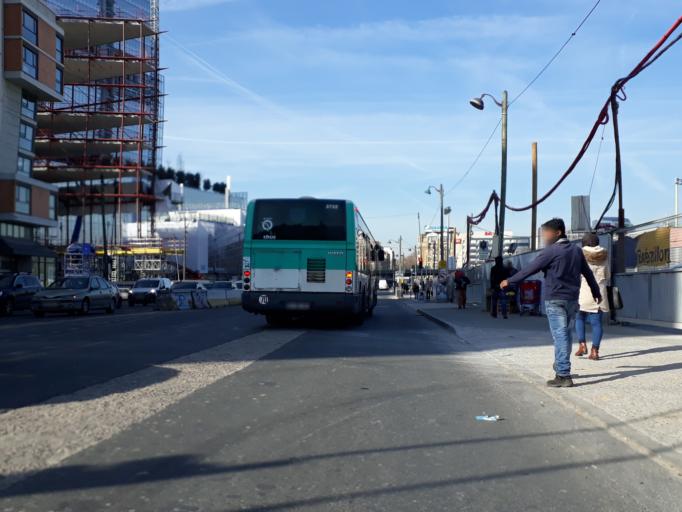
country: FR
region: Ile-de-France
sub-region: Departement des Hauts-de-Seine
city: Clichy
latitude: 48.8948
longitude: 2.3128
